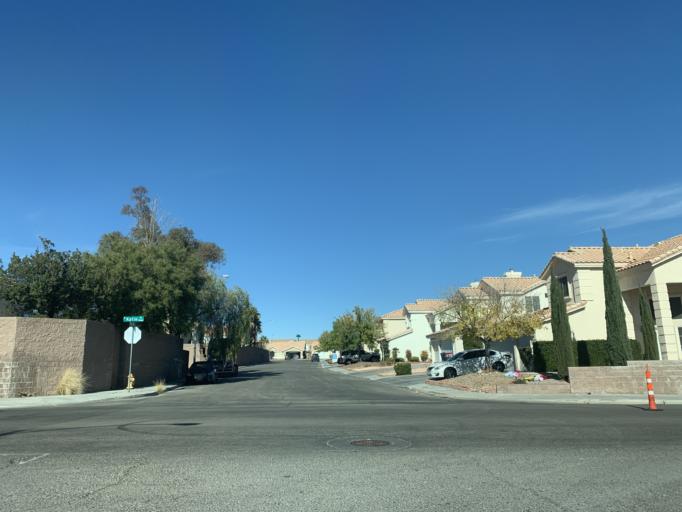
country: US
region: Nevada
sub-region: Clark County
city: Summerlin South
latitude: 36.1206
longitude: -115.3084
